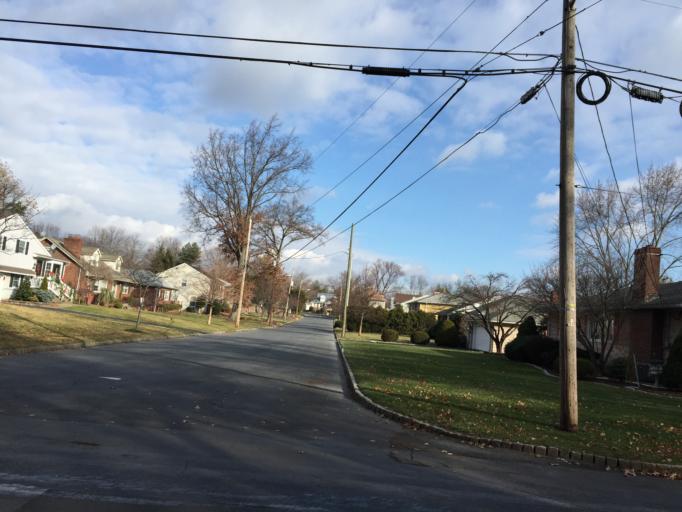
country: US
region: New Jersey
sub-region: Union County
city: Springfield
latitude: 40.7115
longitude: -74.3424
